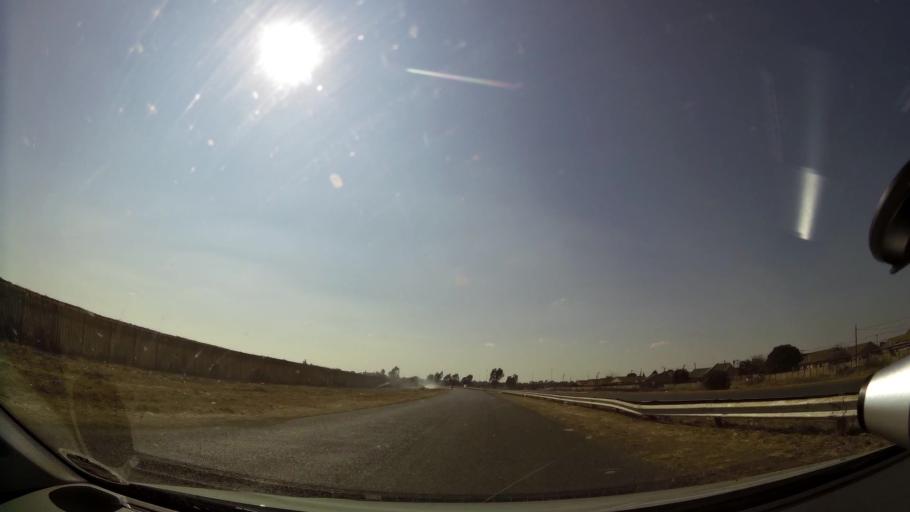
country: ZA
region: Orange Free State
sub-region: Mangaung Metropolitan Municipality
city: Bloemfontein
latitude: -29.1495
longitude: 26.2631
